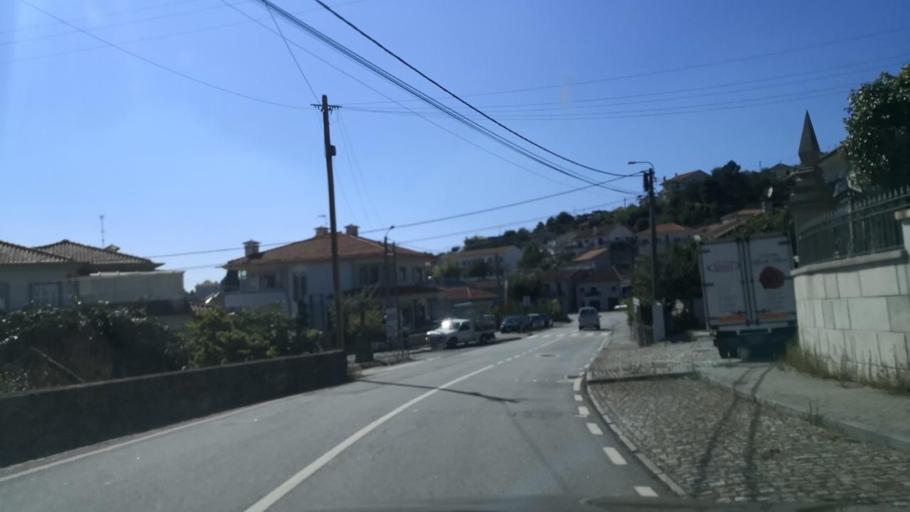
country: PT
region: Braga
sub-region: Fafe
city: Fafe
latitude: 41.4803
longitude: -8.1130
